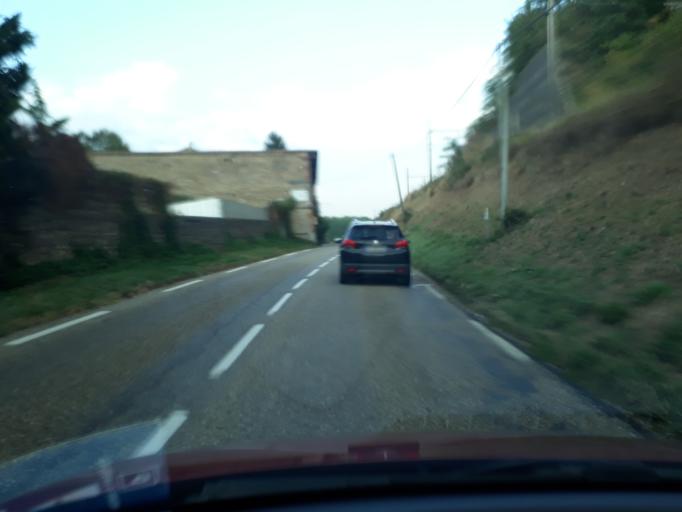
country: FR
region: Rhone-Alpes
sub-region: Departement du Rhone
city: Ampuis
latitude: 45.4724
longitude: 4.7930
